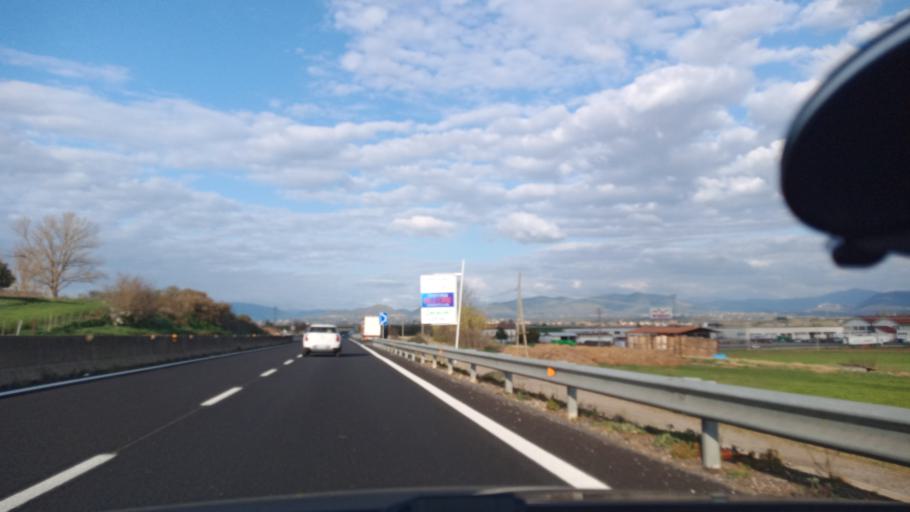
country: IT
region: Latium
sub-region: Citta metropolitana di Roma Capitale
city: Fiano Romano
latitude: 42.1446
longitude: 12.6159
